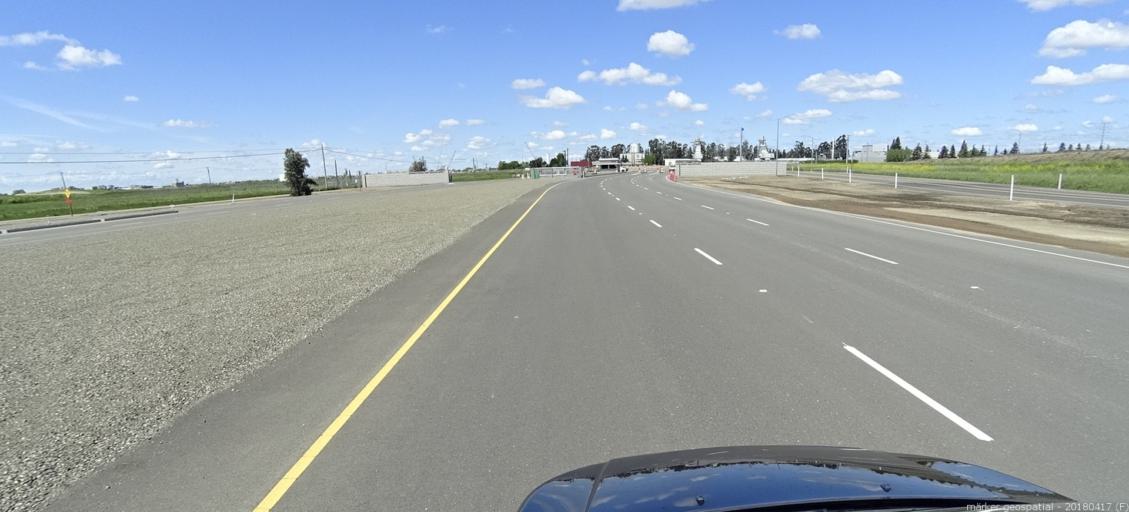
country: US
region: California
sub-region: Sacramento County
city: Laguna
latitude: 38.4413
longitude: -121.4631
